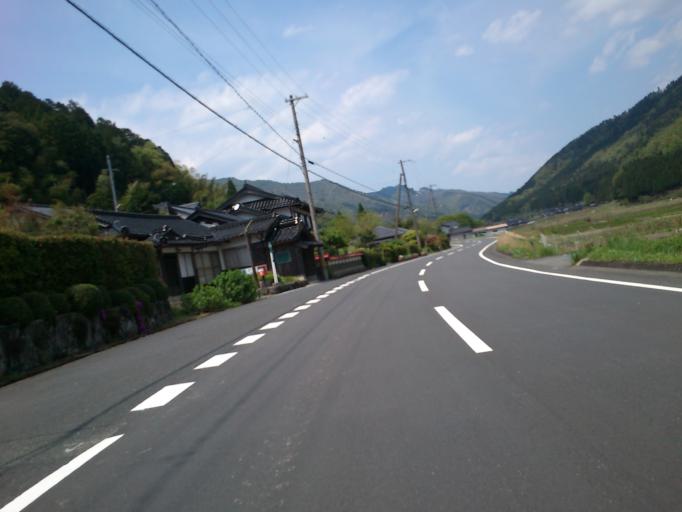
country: JP
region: Kyoto
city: Fukuchiyama
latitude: 35.3571
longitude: 134.9402
